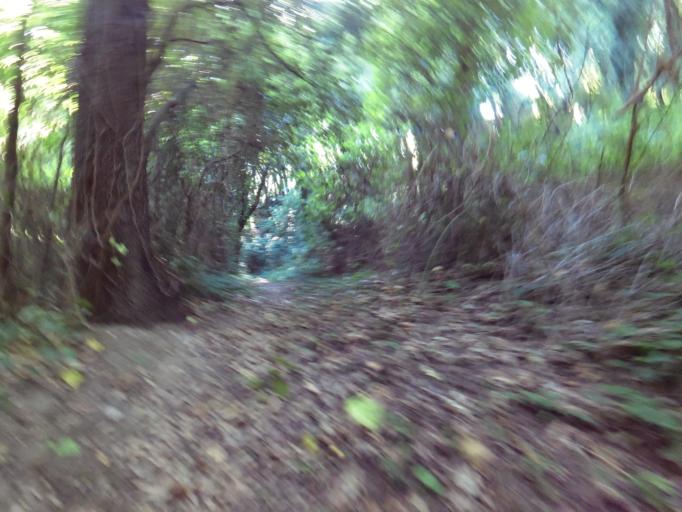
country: IT
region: Calabria
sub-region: Provincia di Reggio Calabria
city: Pazzano
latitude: 38.4764
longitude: 16.4454
